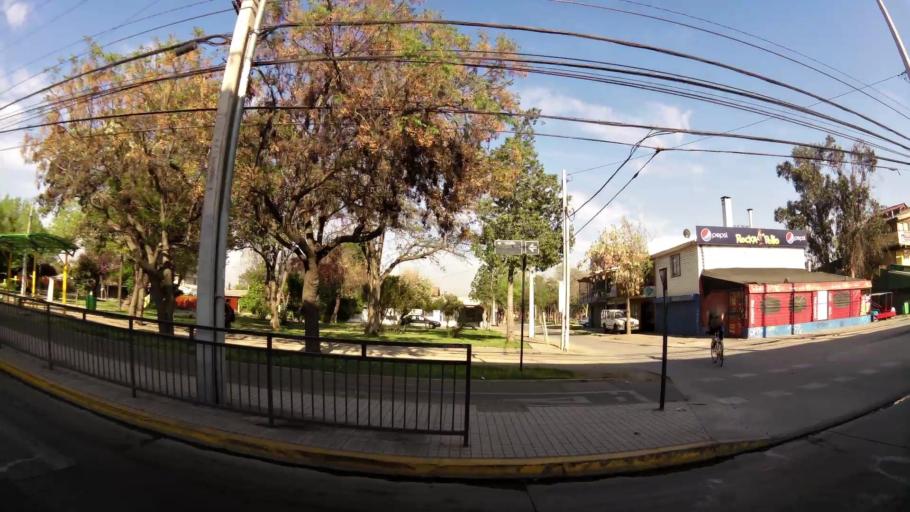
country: CL
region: Santiago Metropolitan
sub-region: Provincia de Cordillera
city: Puente Alto
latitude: -33.5636
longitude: -70.5850
